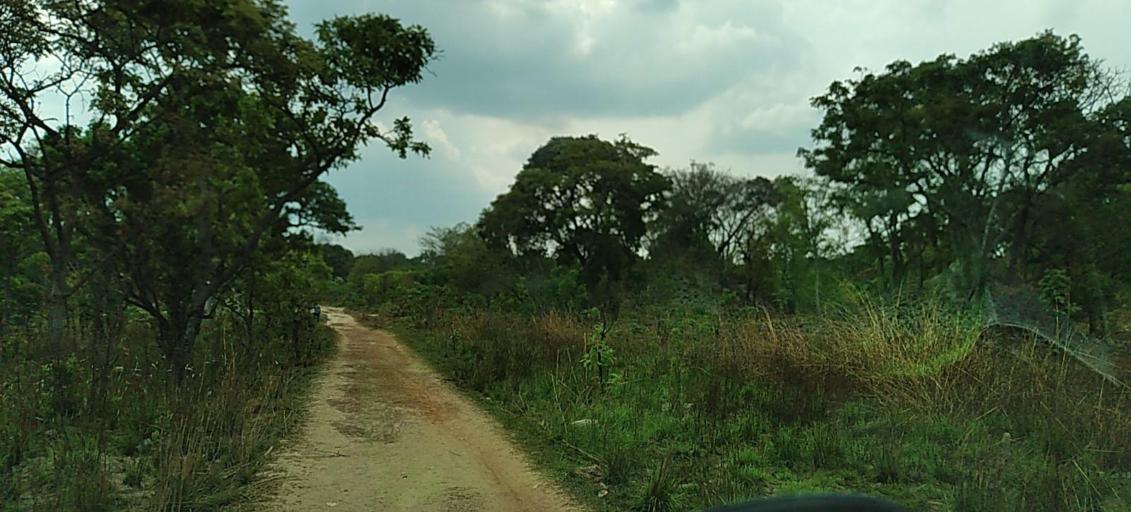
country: ZM
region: North-Western
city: Solwezi
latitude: -12.7871
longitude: 26.5215
